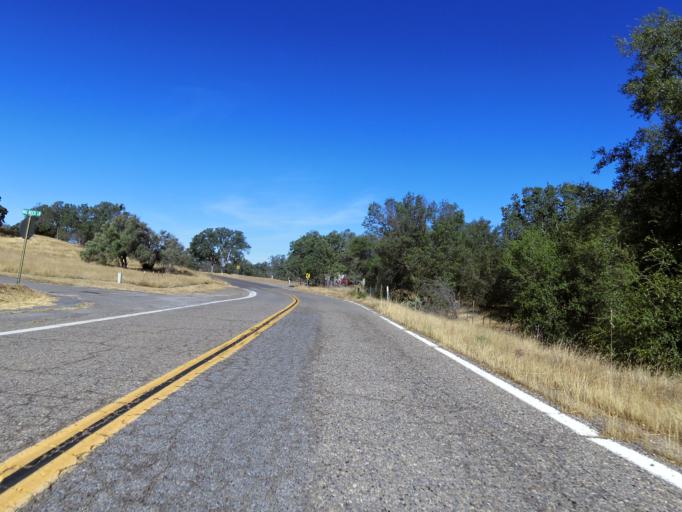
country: US
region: California
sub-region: Madera County
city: Yosemite Lakes
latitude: 37.1933
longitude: -119.8135
